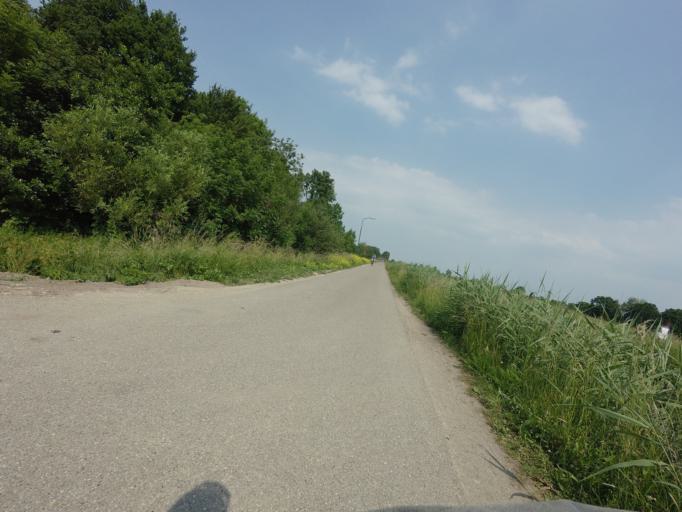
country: NL
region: Utrecht
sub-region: Stichtse Vecht
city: Maarssen
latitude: 52.1543
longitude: 5.0399
